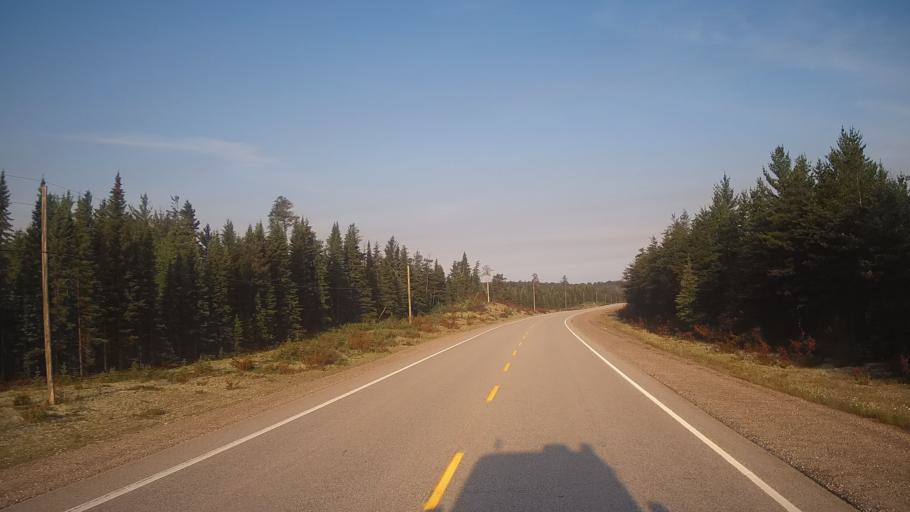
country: CA
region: Ontario
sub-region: Rainy River District
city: Atikokan
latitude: 49.2597
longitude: -91.1740
